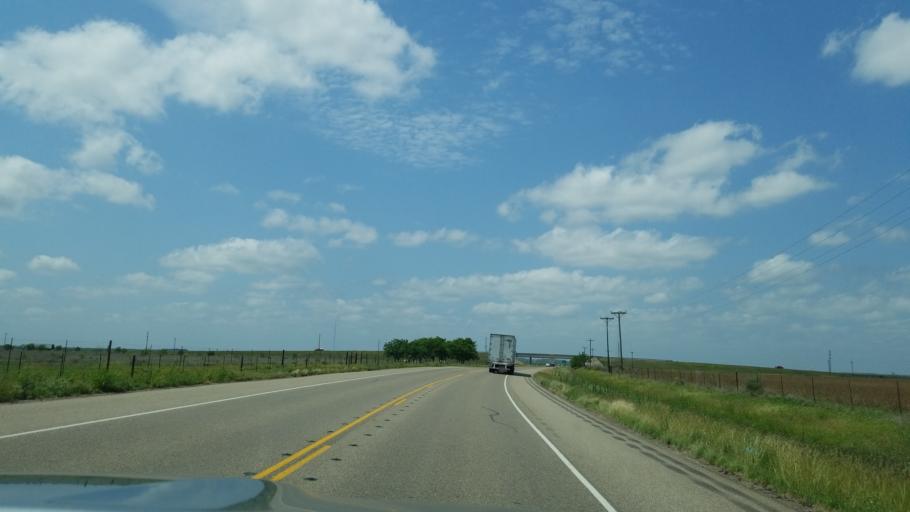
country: US
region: Texas
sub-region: Frio County
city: Pearsall
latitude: 28.9758
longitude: -99.2391
